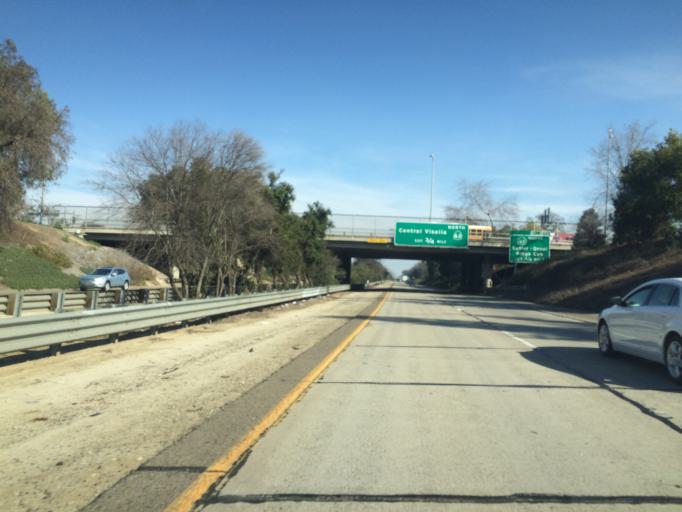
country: US
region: California
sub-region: Tulare County
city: Visalia
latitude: 36.3269
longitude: -119.3151
